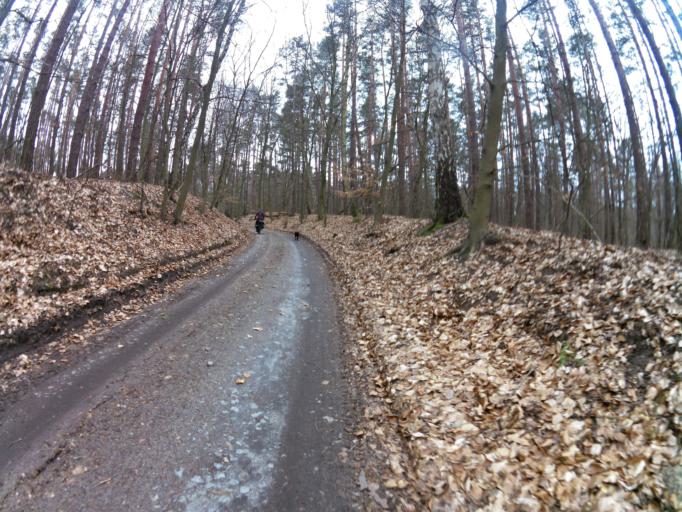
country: PL
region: West Pomeranian Voivodeship
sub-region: Powiat mysliborski
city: Debno
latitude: 52.7497
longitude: 14.7876
